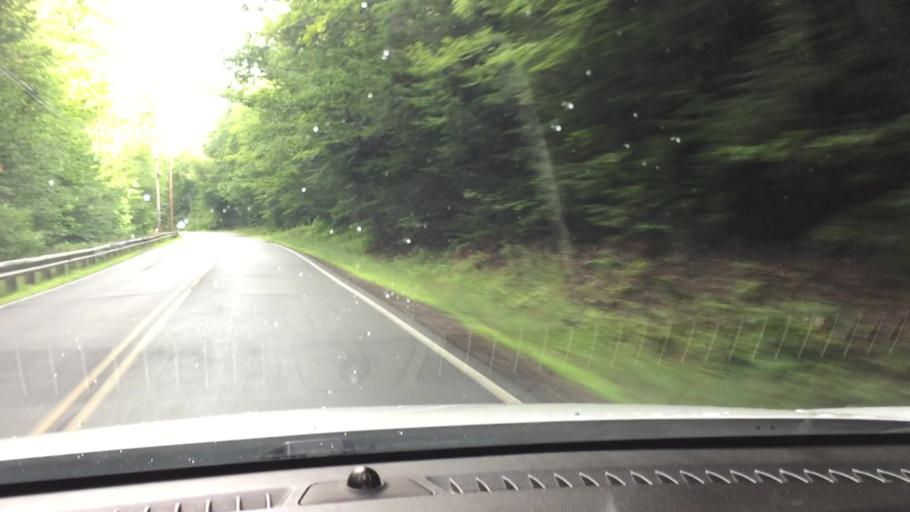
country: US
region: Massachusetts
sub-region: Berkshire County
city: Becket
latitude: 42.4247
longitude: -72.9935
